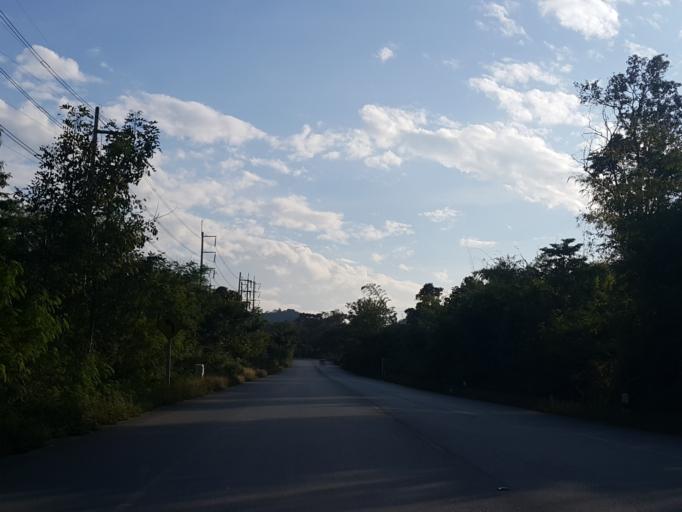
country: TH
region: Lampang
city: Chae Hom
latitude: 18.5265
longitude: 99.5581
